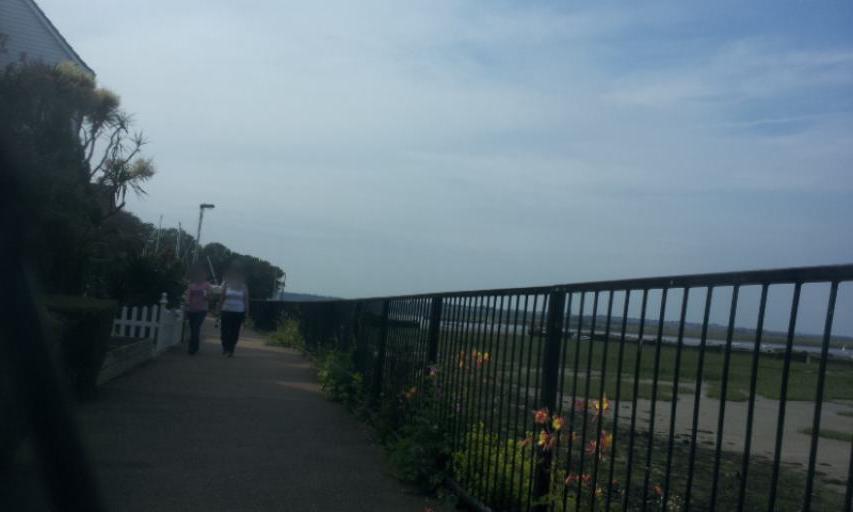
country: GB
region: England
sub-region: Kent
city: Gillingham
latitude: 51.3923
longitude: 0.5704
